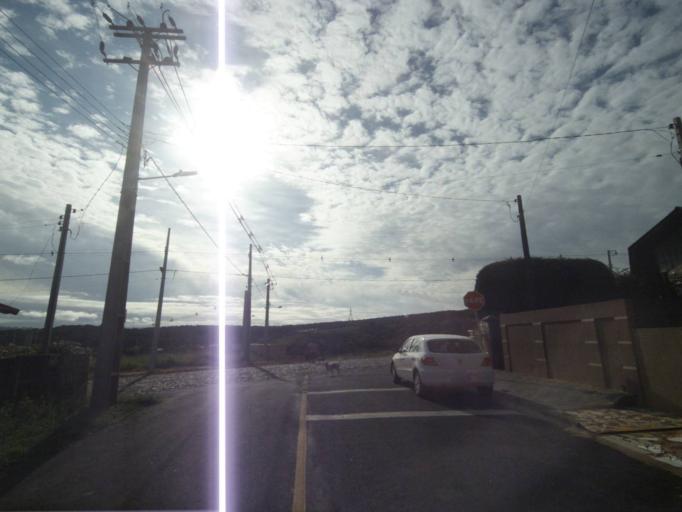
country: BR
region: Parana
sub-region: Telemaco Borba
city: Telemaco Borba
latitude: -24.3456
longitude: -50.6072
